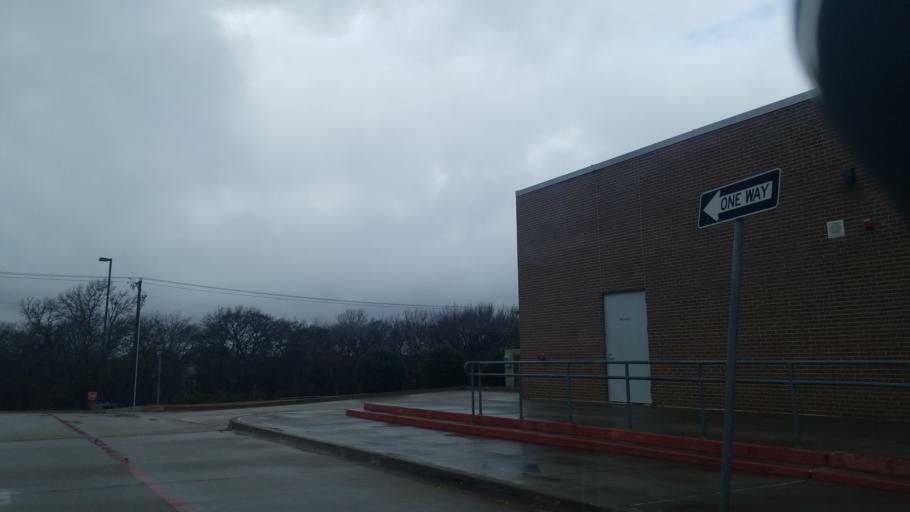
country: US
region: Texas
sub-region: Denton County
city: Corinth
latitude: 33.1473
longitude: -97.0845
